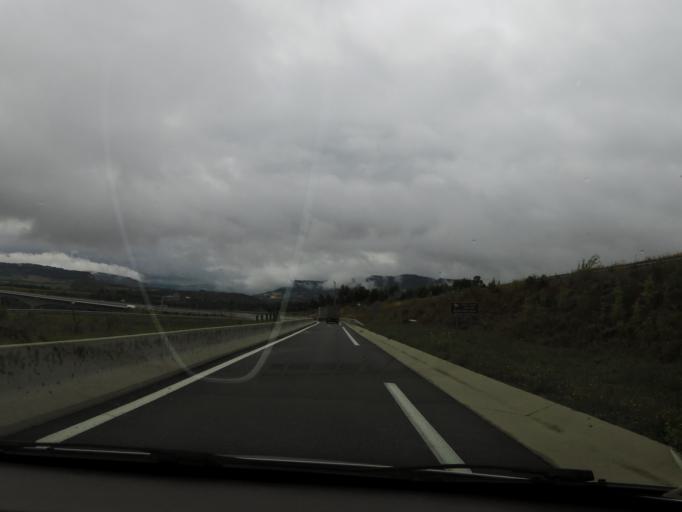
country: FR
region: Languedoc-Roussillon
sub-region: Departement de la Lozere
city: Chirac
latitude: 44.4981
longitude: 3.2398
